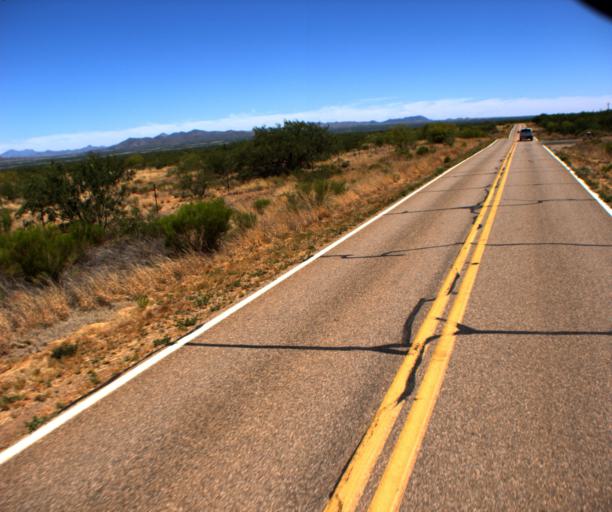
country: US
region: Arizona
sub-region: Pima County
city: Three Points
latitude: 31.6977
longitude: -111.4873
